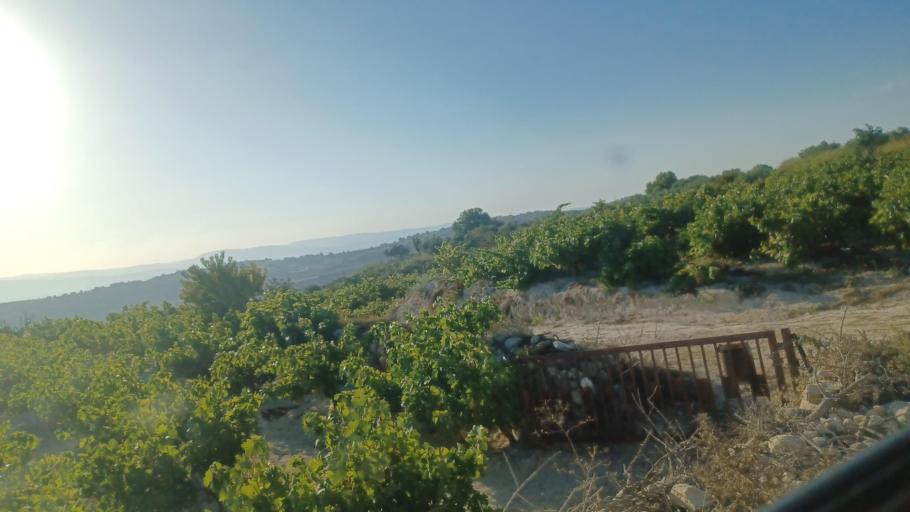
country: CY
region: Pafos
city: Mesogi
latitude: 34.8525
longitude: 32.4717
